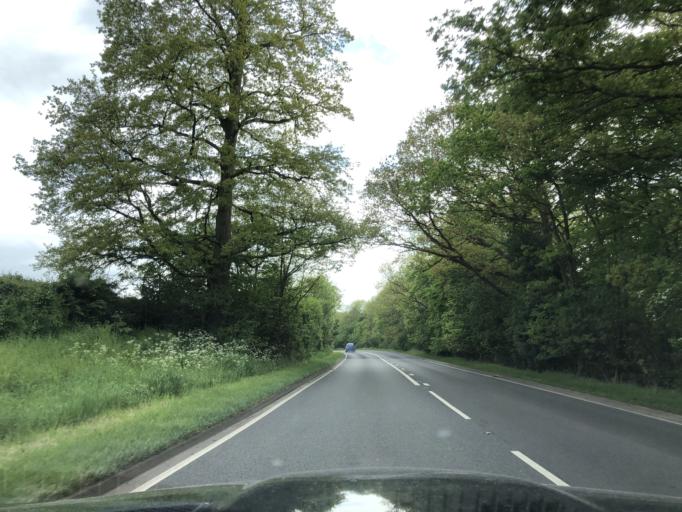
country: GB
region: England
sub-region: Warwickshire
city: Shipston on Stour
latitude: 52.1263
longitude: -1.6178
